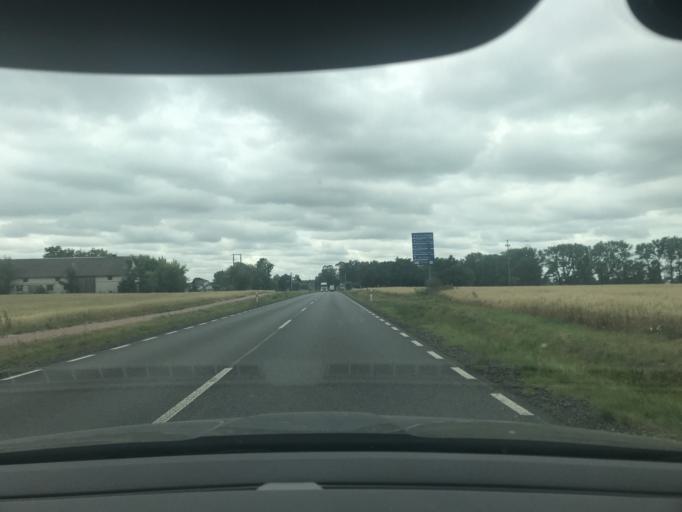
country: PL
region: Lodz Voivodeship
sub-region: Powiat poddebicki
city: Wartkowice
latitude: 51.9767
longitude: 19.0228
